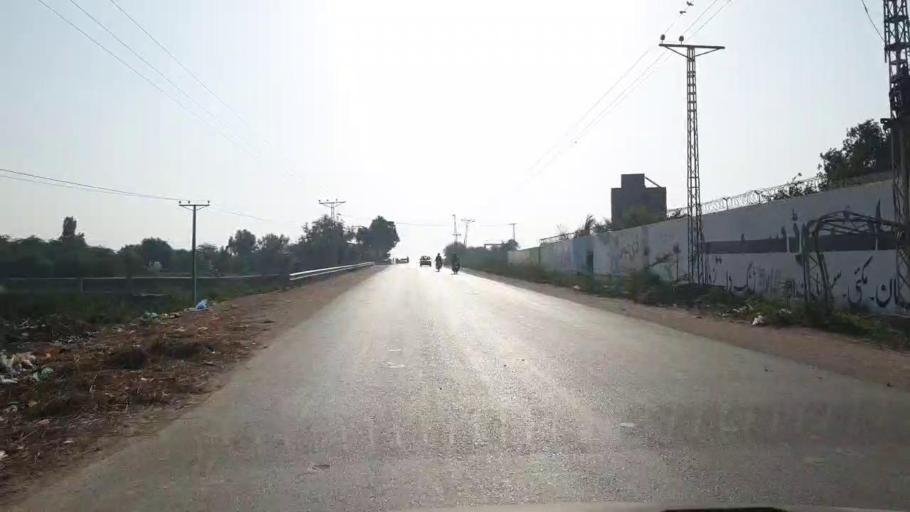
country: PK
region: Sindh
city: Badin
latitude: 24.6758
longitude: 68.8495
